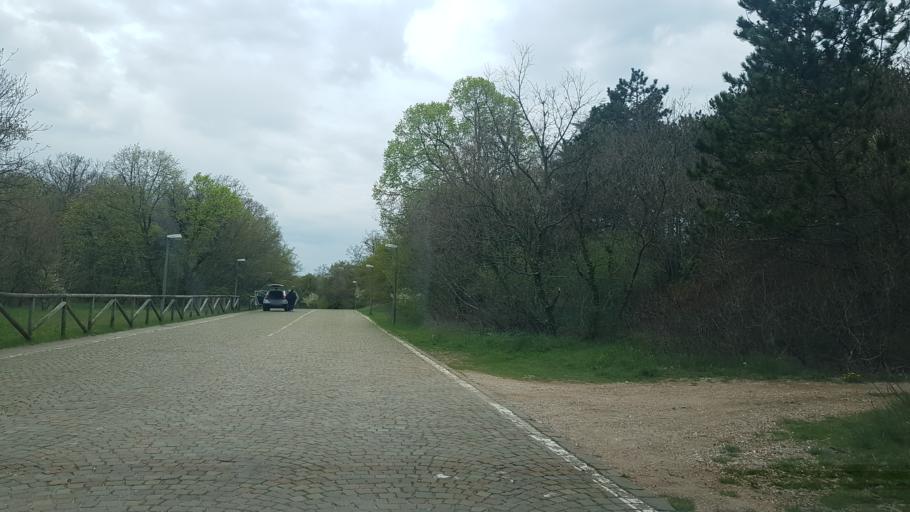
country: IT
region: Friuli Venezia Giulia
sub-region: Provincia di Trieste
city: Domio
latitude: 45.6477
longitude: 13.8464
